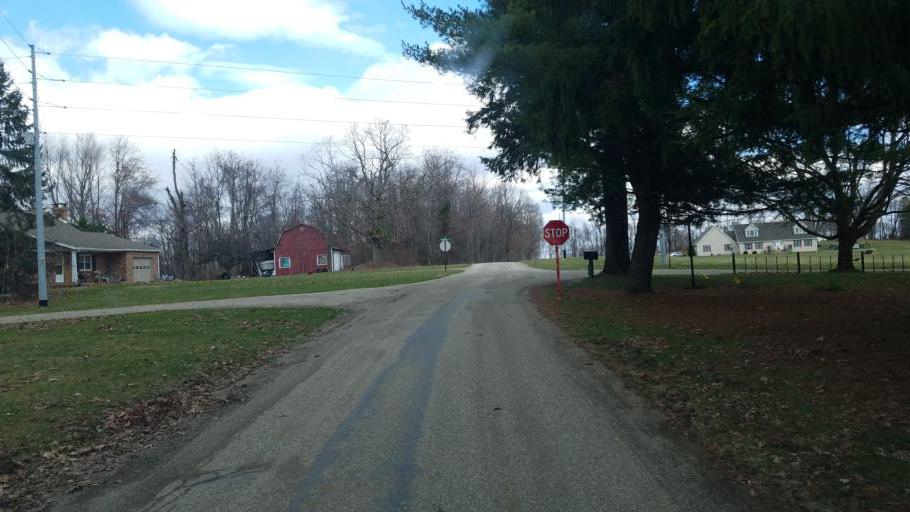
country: US
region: Ohio
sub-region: Sandusky County
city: Bellville
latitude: 40.5797
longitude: -82.4843
